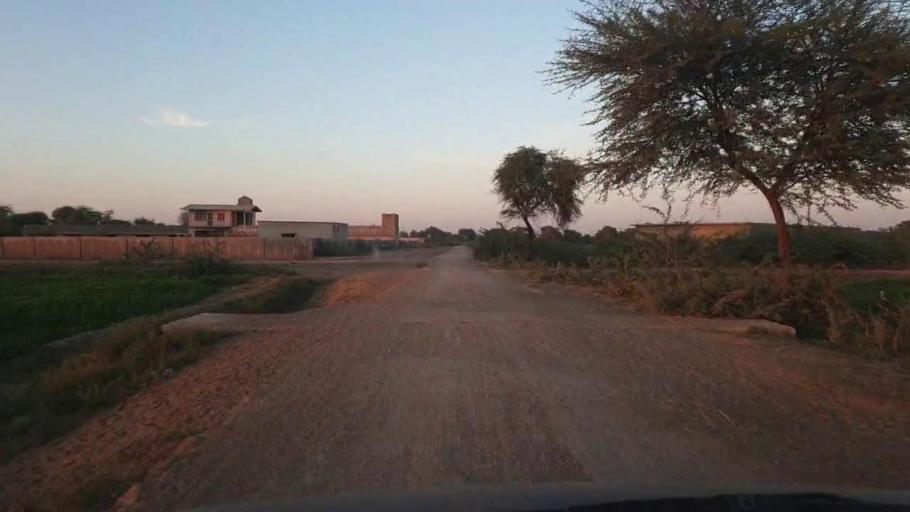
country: PK
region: Sindh
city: Umarkot
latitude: 25.3734
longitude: 69.7082
